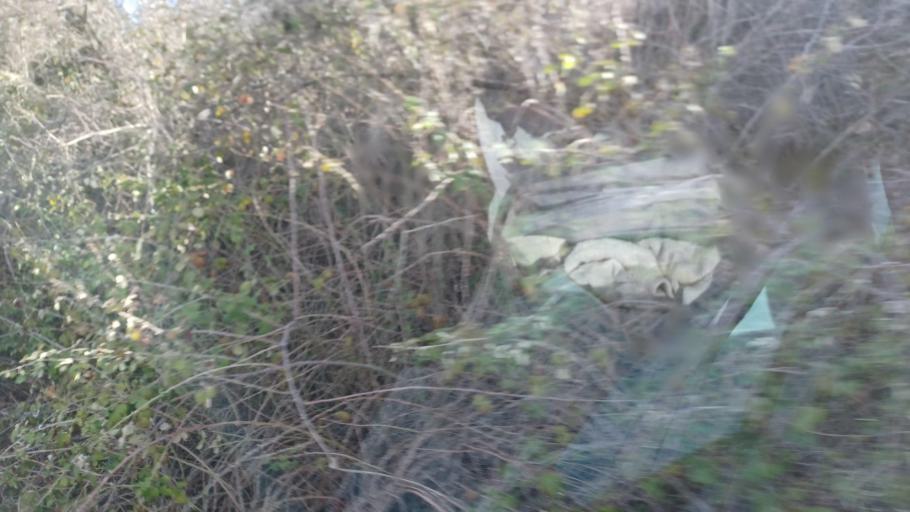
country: CY
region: Limassol
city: Pachna
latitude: 34.8459
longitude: 32.8112
